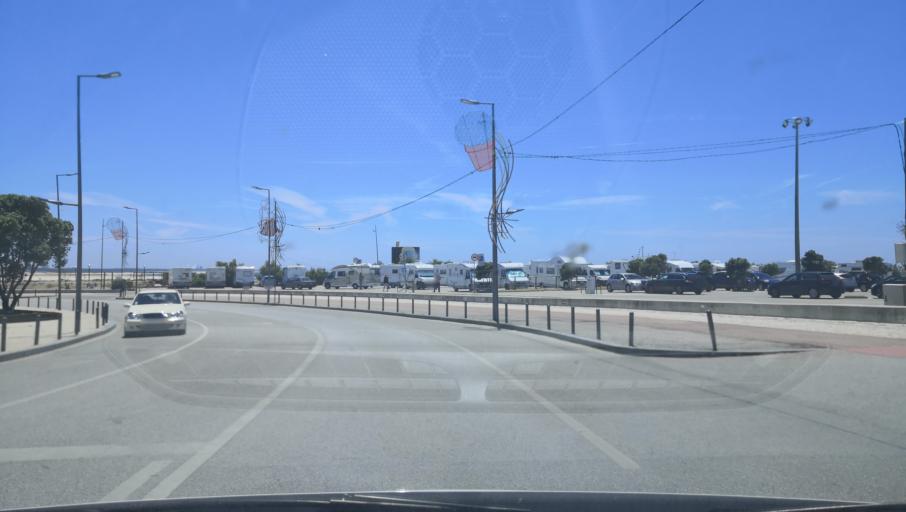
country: PT
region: Coimbra
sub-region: Figueira da Foz
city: Figueira da Foz
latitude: 40.1485
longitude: -8.8670
